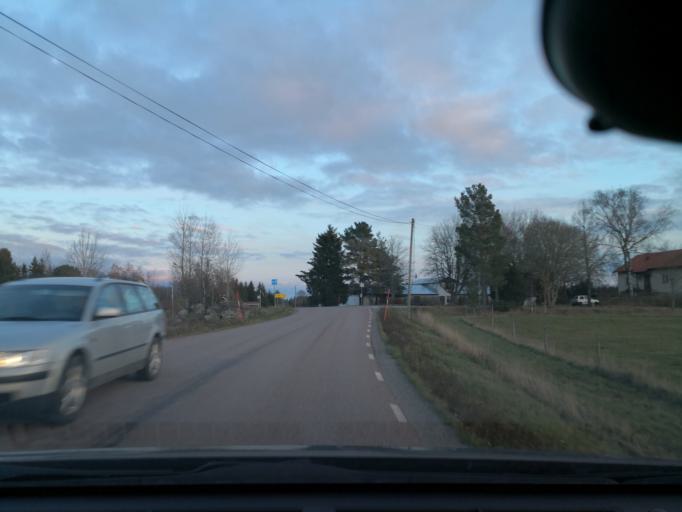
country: SE
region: Uppsala
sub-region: Enkopings Kommun
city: Irsta
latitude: 59.6815
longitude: 16.8140
